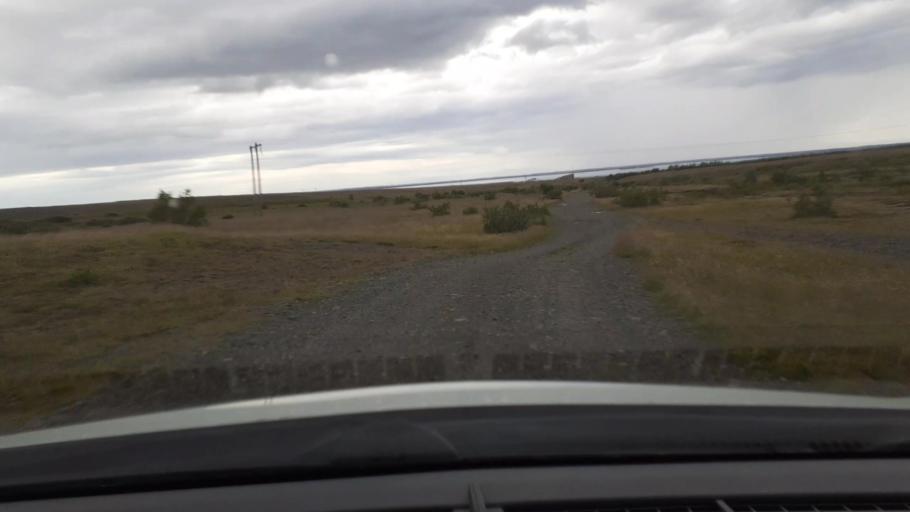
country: IS
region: West
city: Borgarnes
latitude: 64.4611
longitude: -21.9552
